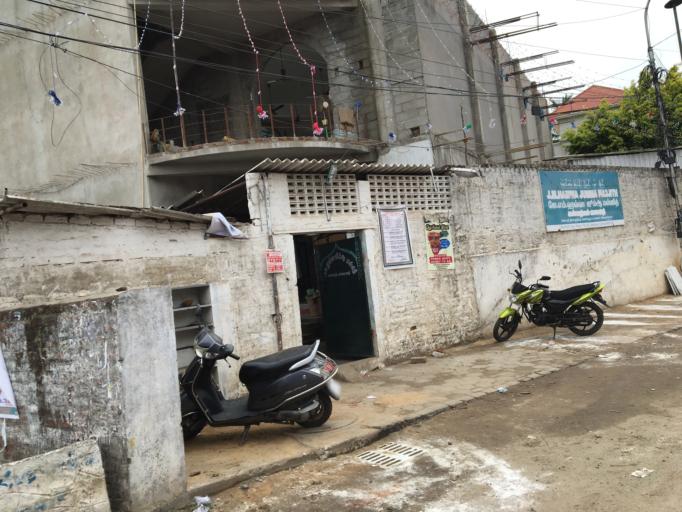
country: IN
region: Tamil Nadu
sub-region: Kancheepuram
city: Alandur
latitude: 12.9890
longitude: 80.2151
